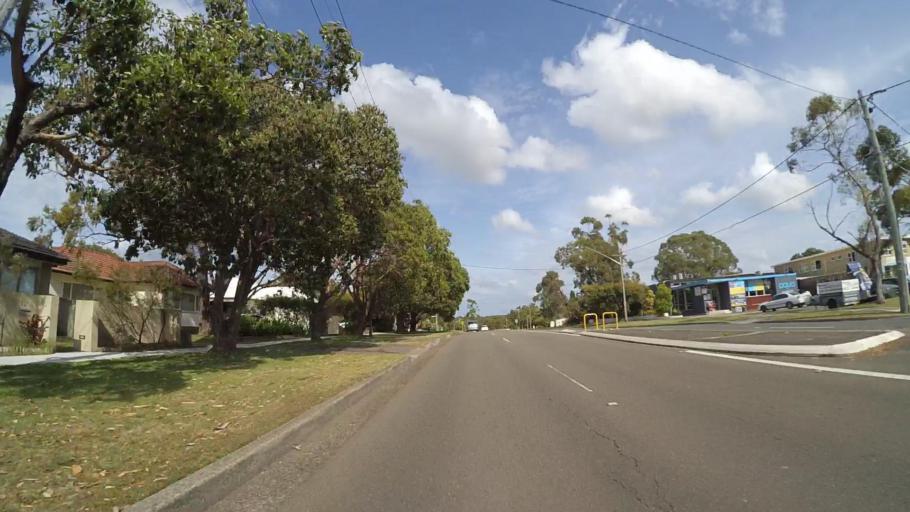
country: AU
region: New South Wales
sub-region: Sutherland Shire
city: Miranda
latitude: -34.0413
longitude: 151.1087
